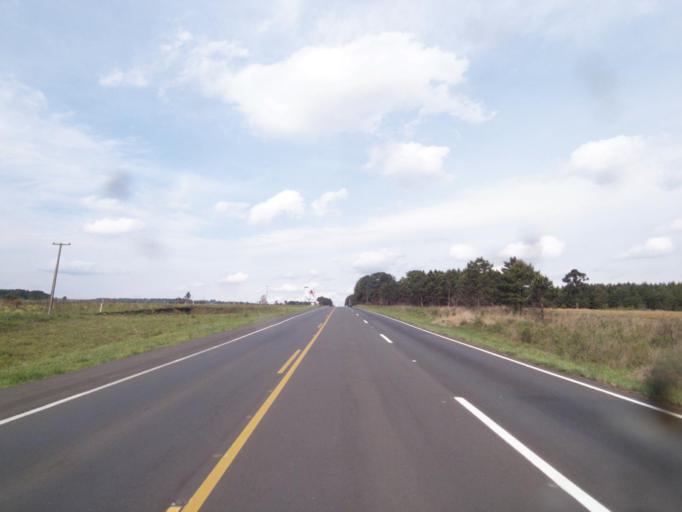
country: BR
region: Parana
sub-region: Campo Largo
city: Campo Largo
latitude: -25.4655
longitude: -49.7462
